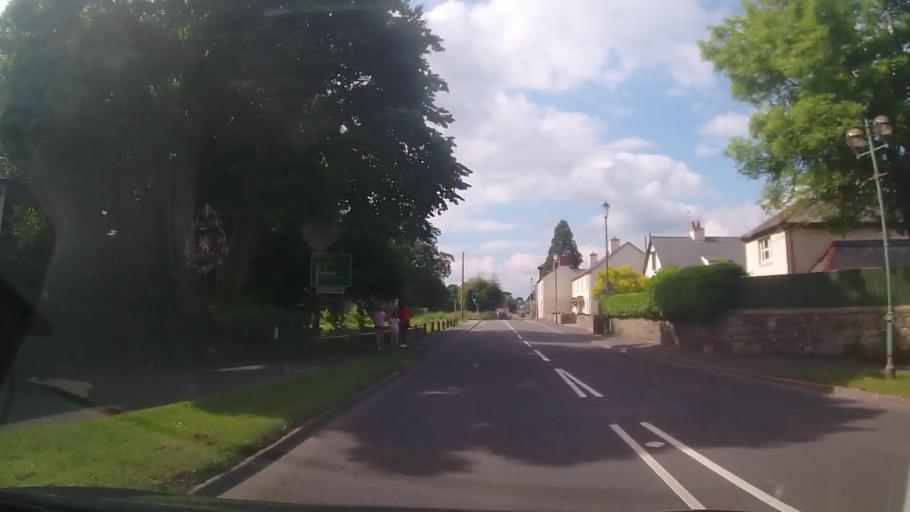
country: GB
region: England
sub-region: Shropshire
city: Whittington
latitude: 52.8732
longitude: -3.0015
